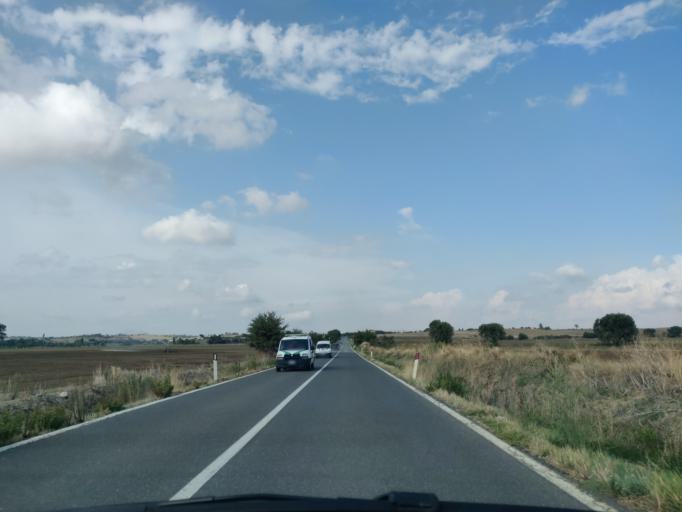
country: IT
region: Latium
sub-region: Provincia di Viterbo
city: Tarquinia
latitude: 42.2162
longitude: 11.7831
